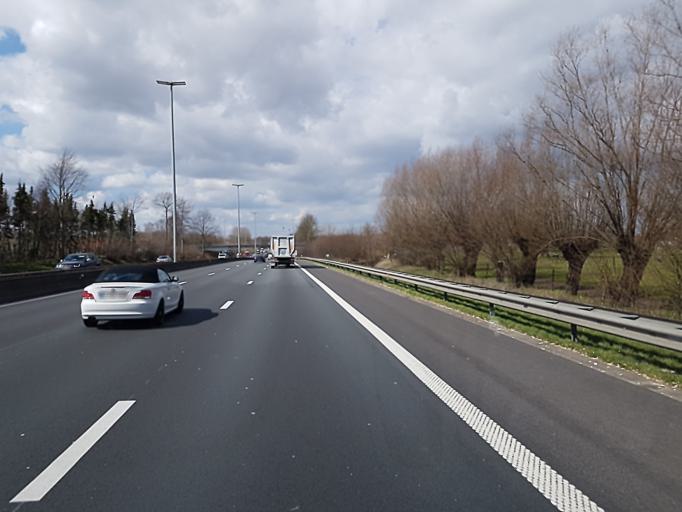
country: BE
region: Flanders
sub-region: Provincie Oost-Vlaanderen
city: Sint-Lievens-Houtem
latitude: 50.9634
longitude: 3.8588
